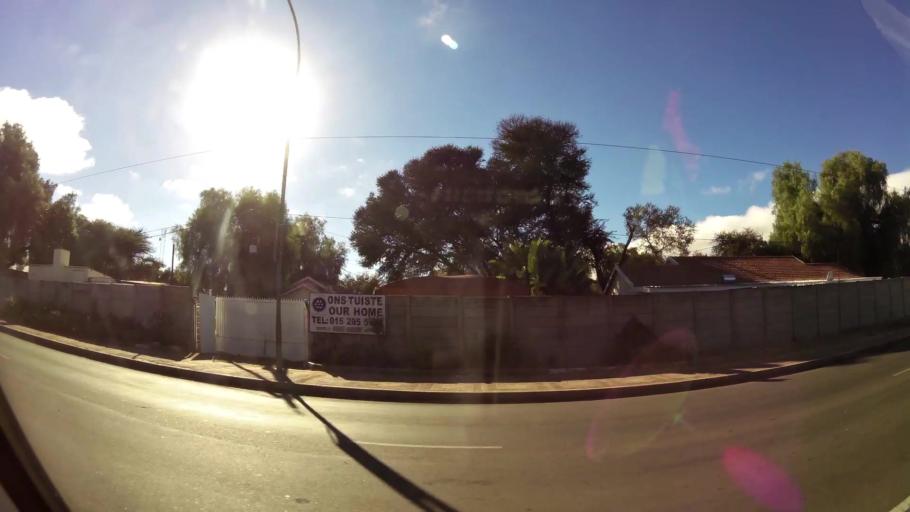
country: ZA
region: Limpopo
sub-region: Capricorn District Municipality
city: Polokwane
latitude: -23.9202
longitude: 29.4625
